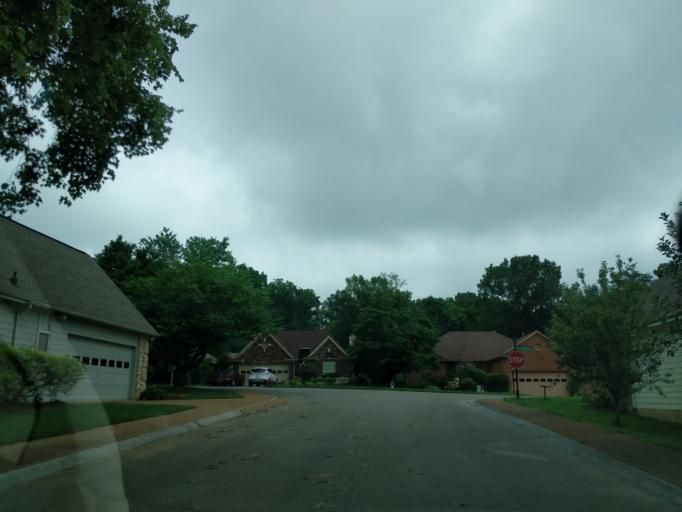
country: US
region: Tennessee
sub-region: Davidson County
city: Lakewood
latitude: 36.1731
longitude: -86.6184
